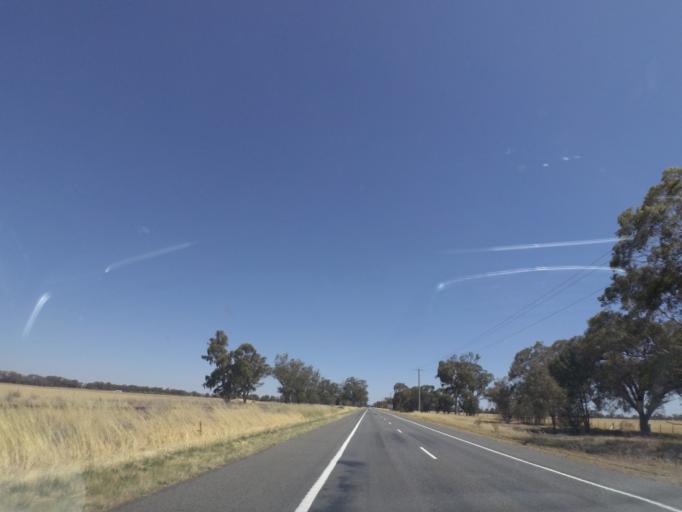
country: AU
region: Victoria
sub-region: Greater Shepparton
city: Shepparton
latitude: -36.2053
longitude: 145.4319
